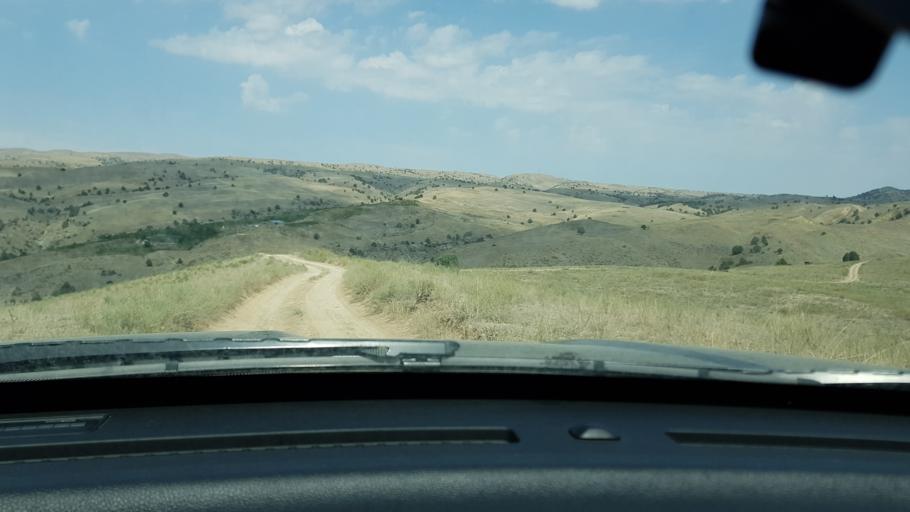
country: TM
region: Ahal
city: Baharly
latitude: 38.4096
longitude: 56.9216
